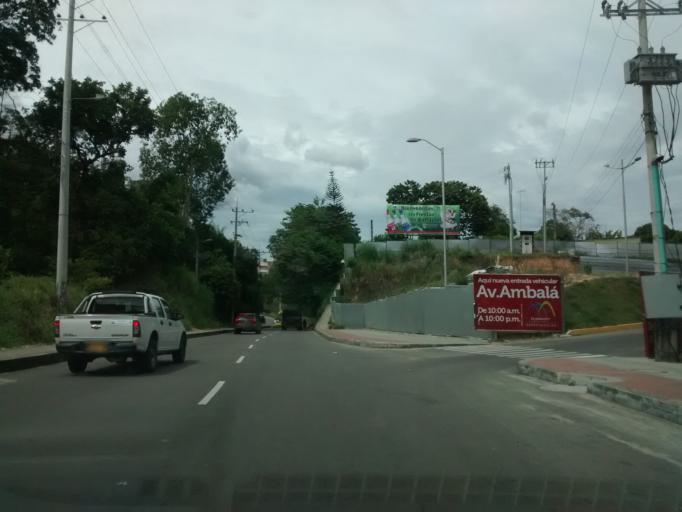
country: CO
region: Tolima
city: Ibague
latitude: 4.4466
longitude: -75.2048
